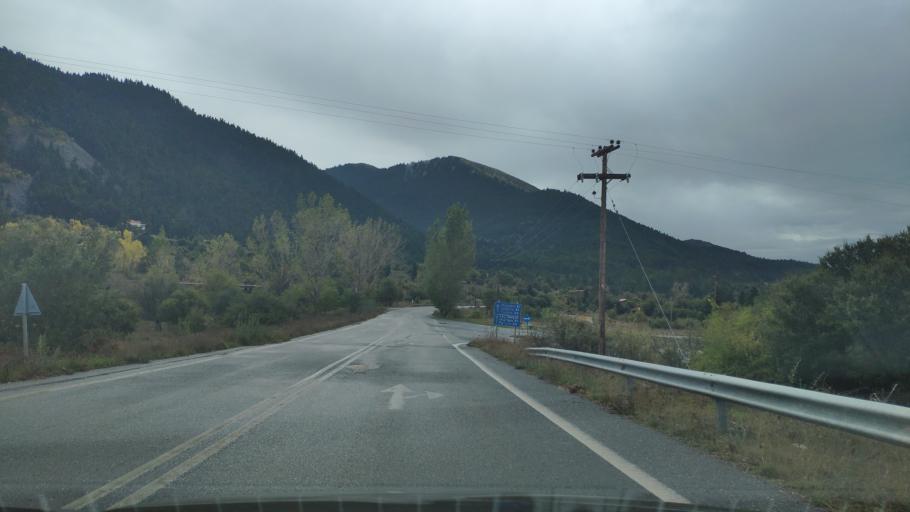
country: GR
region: Peloponnese
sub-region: Nomos Arkadias
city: Dimitsana
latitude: 37.6559
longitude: 22.1878
